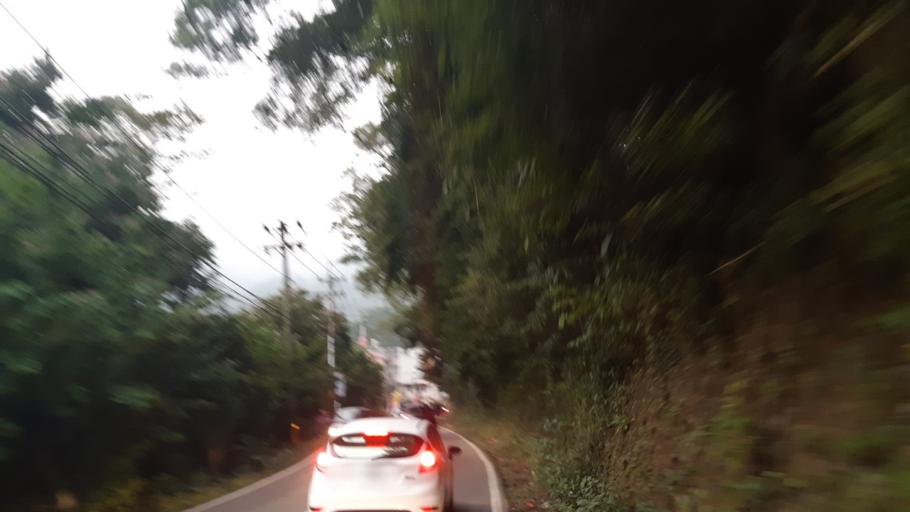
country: TW
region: Taiwan
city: Daxi
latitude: 24.7054
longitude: 121.2098
